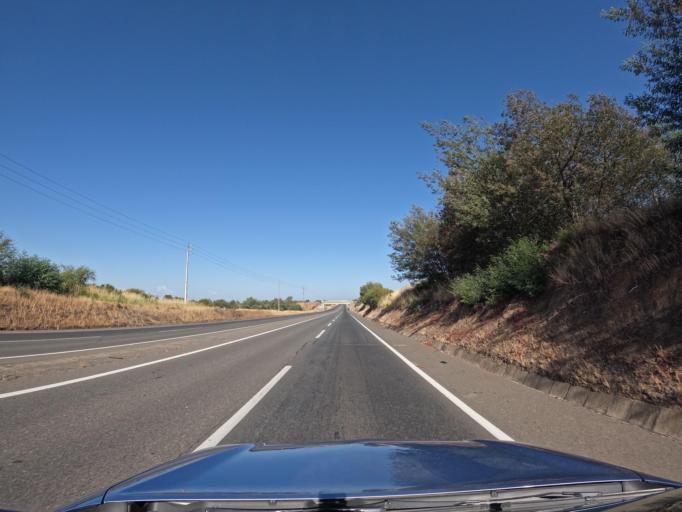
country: CL
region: Biobio
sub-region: Provincia de Nuble
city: Bulnes
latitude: -36.6588
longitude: -72.2866
